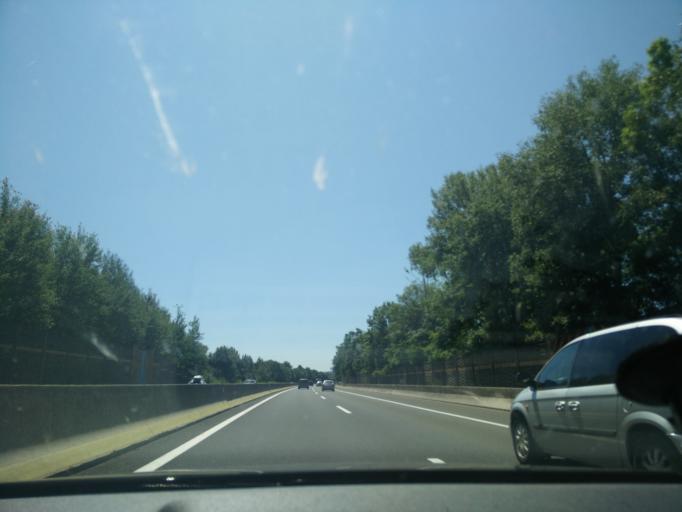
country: AT
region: Styria
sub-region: Politischer Bezirk Hartberg-Fuerstenfeld
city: Sebersdorf
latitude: 47.2236
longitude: 15.9954
